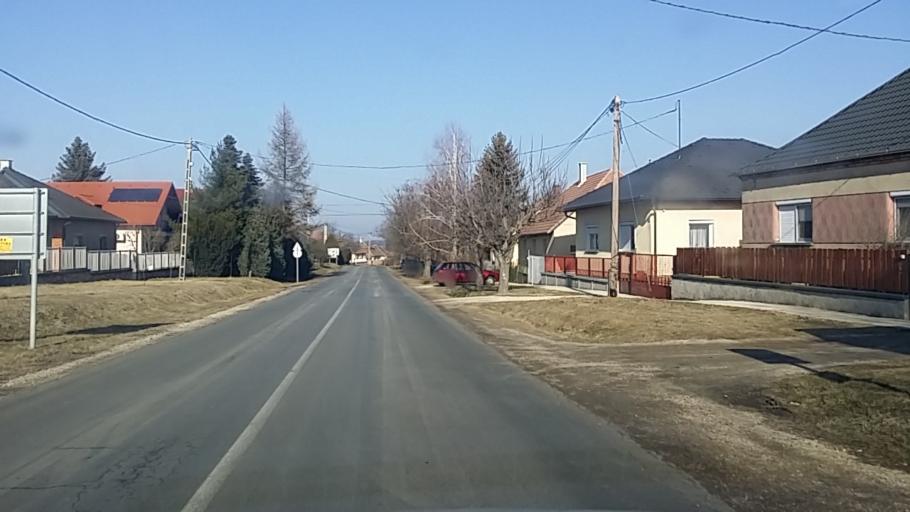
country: HU
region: Komarom-Esztergom
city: Bokod
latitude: 47.5131
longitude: 18.2231
